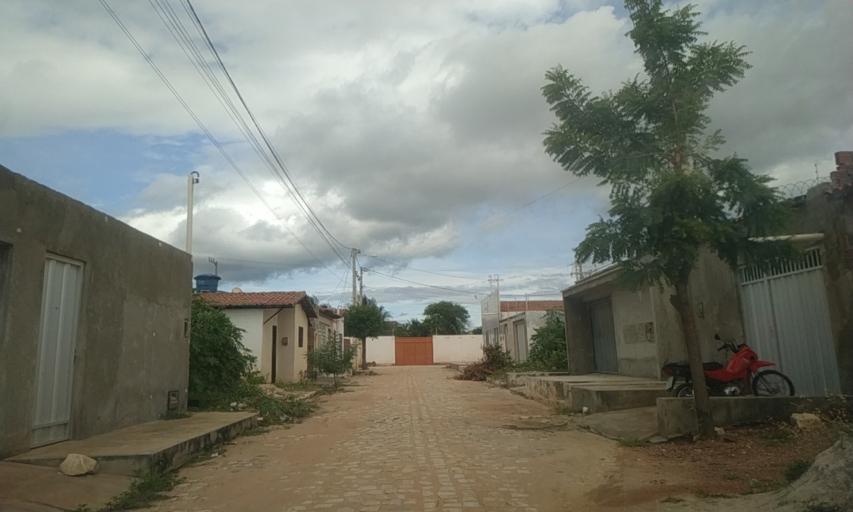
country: BR
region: Rio Grande do Norte
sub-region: Areia Branca
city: Areia Branca
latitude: -4.9517
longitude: -37.1216
